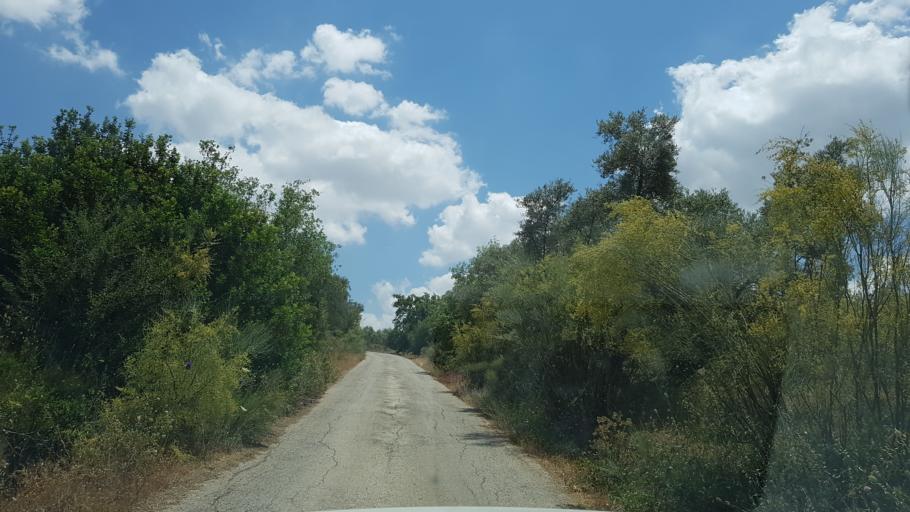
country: ES
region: Andalusia
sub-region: Province of Cordoba
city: Cabra
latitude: 37.5187
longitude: -4.4568
